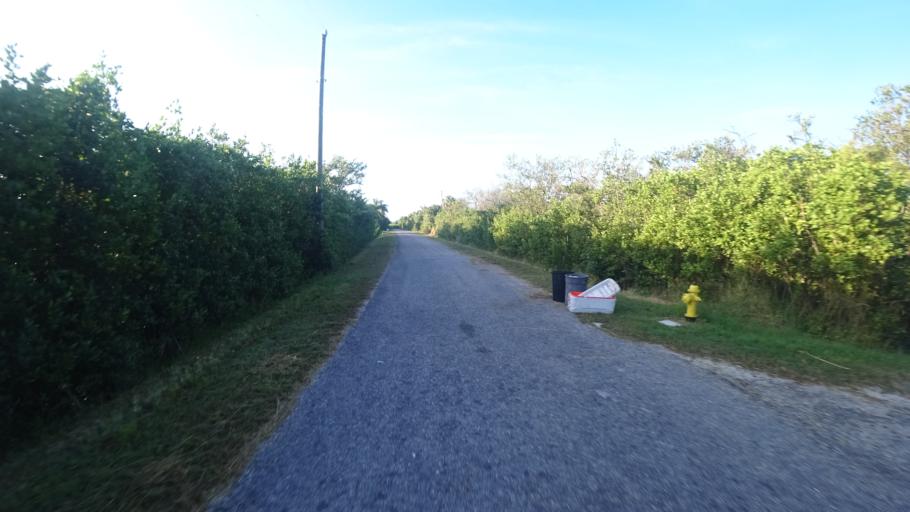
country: US
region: Florida
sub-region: Manatee County
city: Memphis
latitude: 27.5646
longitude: -82.5938
